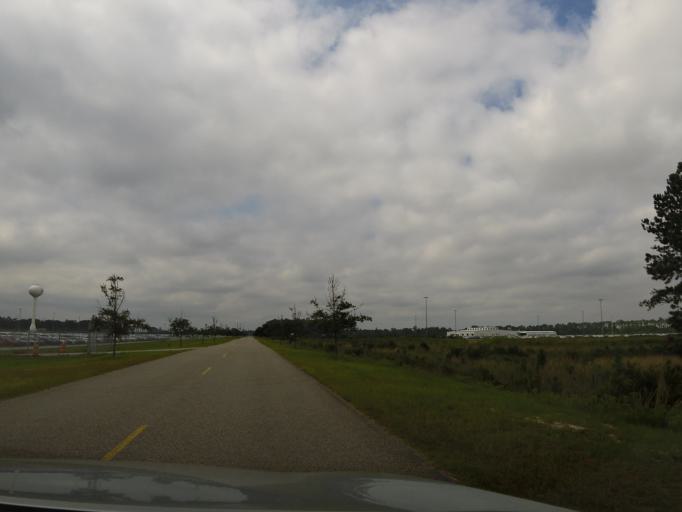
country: US
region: Georgia
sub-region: Glynn County
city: Brunswick
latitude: 31.1057
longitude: -81.5369
